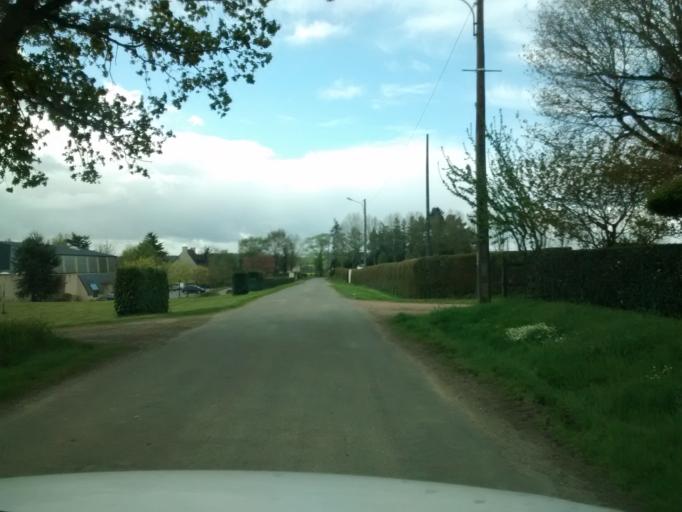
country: FR
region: Brittany
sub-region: Departement du Morbihan
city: Ruffiac
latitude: 47.8188
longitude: -2.2783
